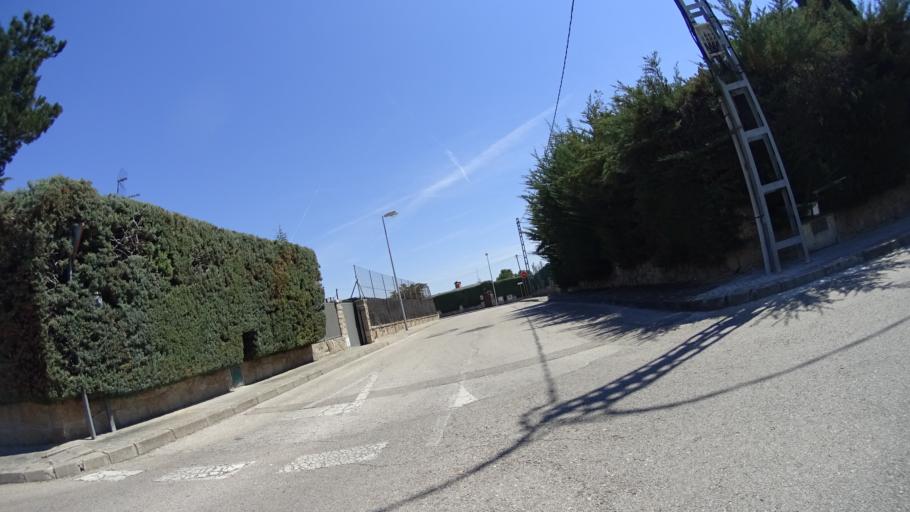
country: ES
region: Madrid
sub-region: Provincia de Madrid
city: Colmenarejo
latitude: 40.5550
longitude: -4.0062
